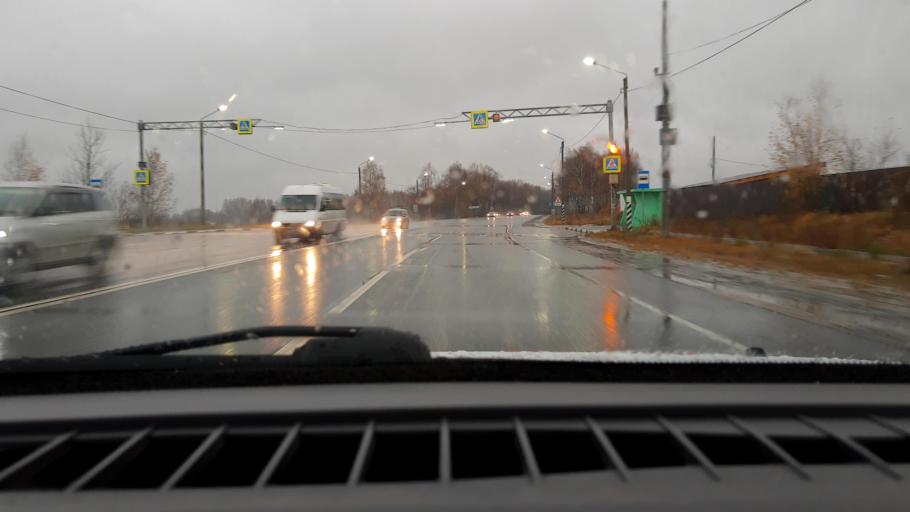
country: RU
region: Nizjnij Novgorod
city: Sitniki
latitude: 56.5065
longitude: 44.0235
